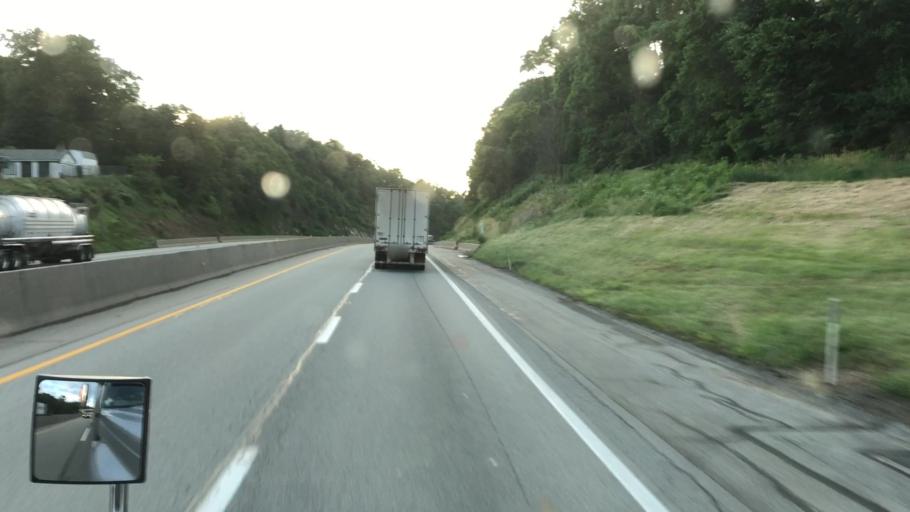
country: US
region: Pennsylvania
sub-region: Fayette County
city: Bear Rocks
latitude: 40.1598
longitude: -79.4812
